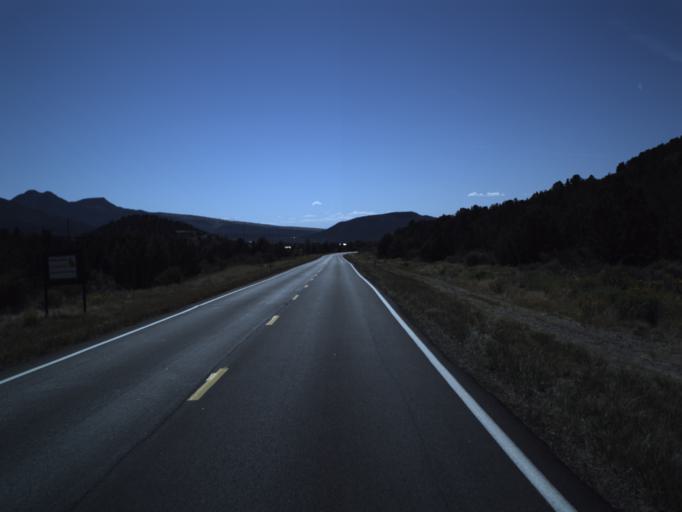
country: US
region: Utah
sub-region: Washington County
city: Enterprise
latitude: 37.4311
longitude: -113.6292
